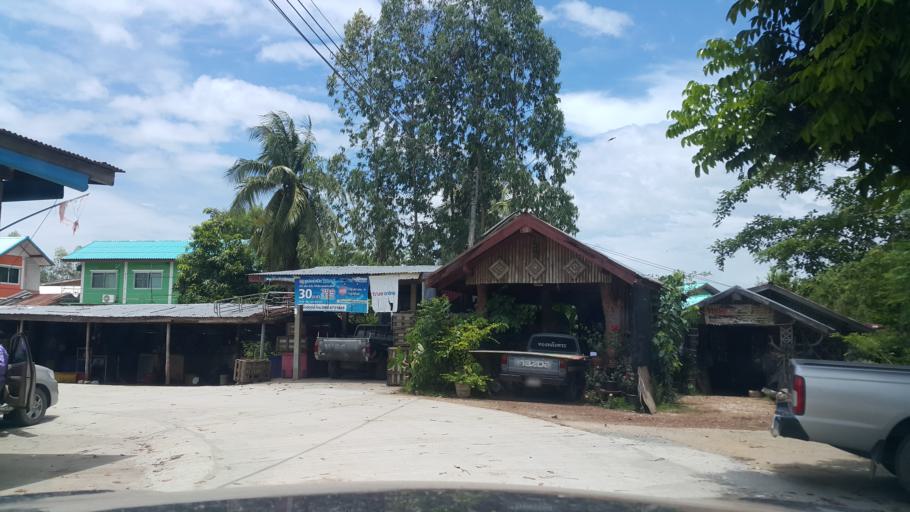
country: TH
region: Sukhothai
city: Kong Krailat
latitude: 16.9311
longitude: 99.9583
